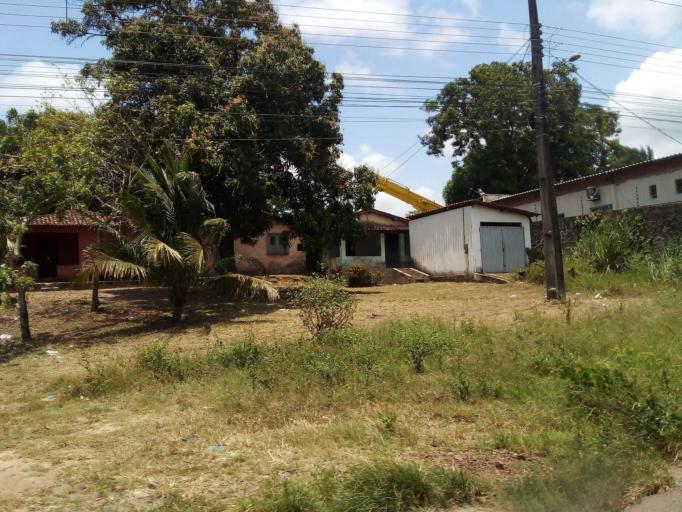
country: BR
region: Maranhao
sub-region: Sao Luis
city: Sao Luis
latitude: -2.6999
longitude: -44.3086
